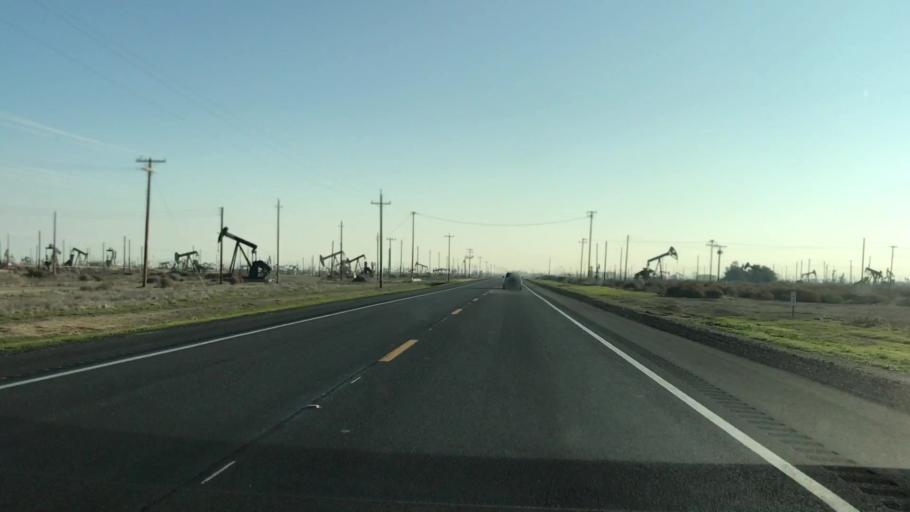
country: US
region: California
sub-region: Kern County
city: Lost Hills
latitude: 35.6157
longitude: -119.7355
